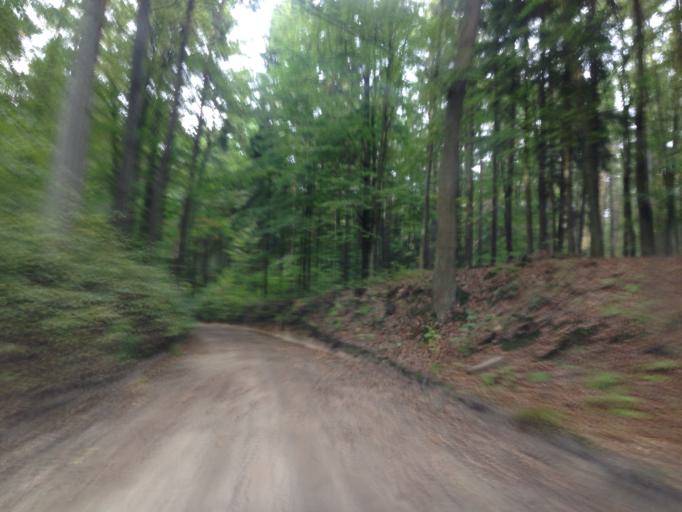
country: PL
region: Warmian-Masurian Voivodeship
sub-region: Powiat ilawski
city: Susz
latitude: 53.7562
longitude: 19.3076
